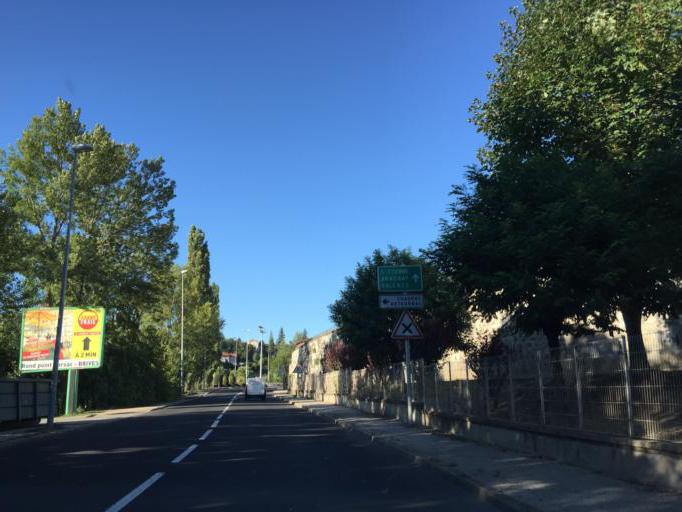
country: FR
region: Auvergne
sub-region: Departement de la Haute-Loire
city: Chadrac
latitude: 45.0542
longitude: 3.9016
